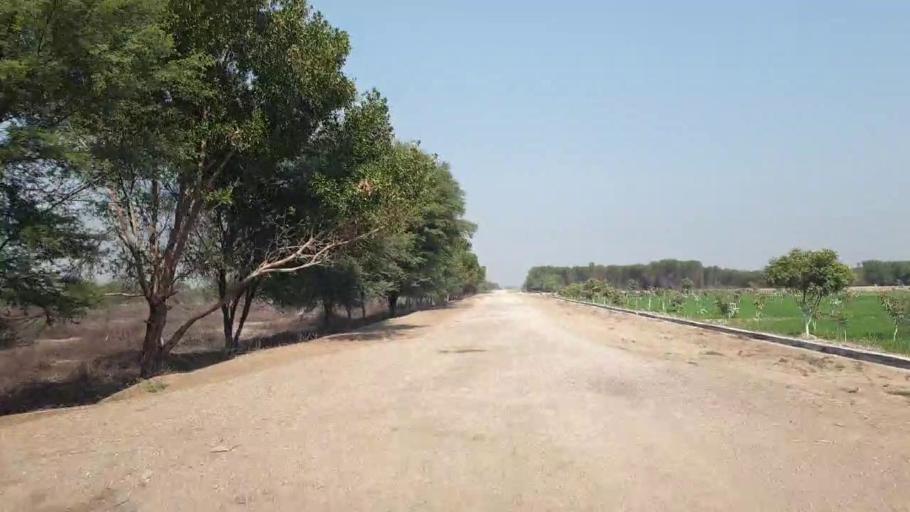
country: PK
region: Sindh
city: Mirwah Gorchani
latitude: 25.3562
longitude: 68.9317
